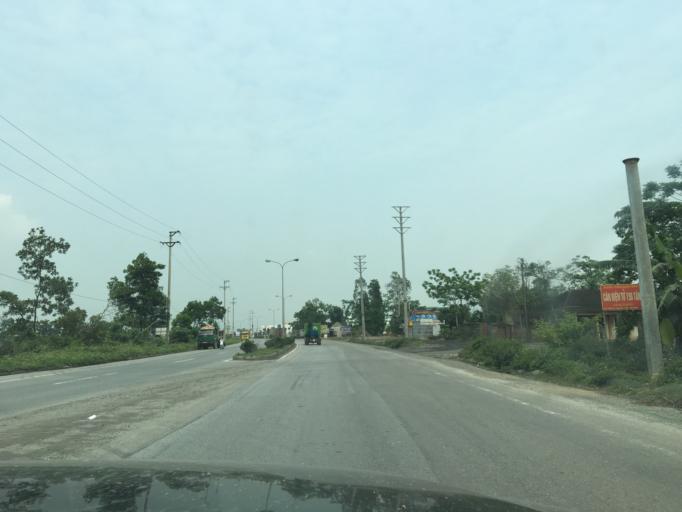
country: VN
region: Ninh Binh
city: Thanh Pho Ninh Binh
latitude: 20.2155
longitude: 105.9794
